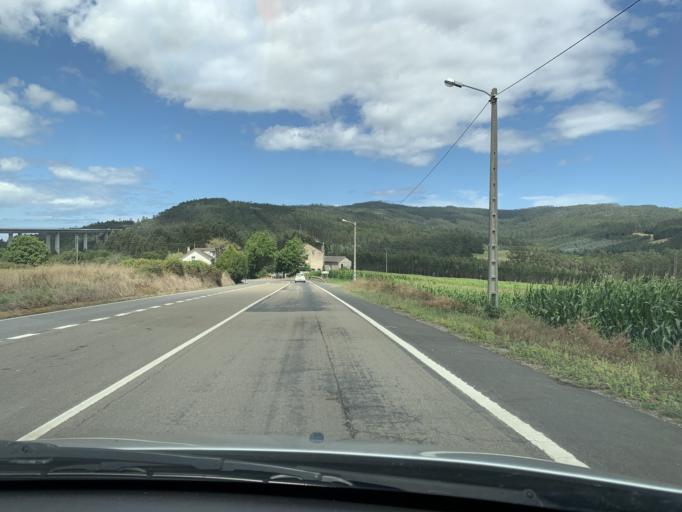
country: ES
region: Galicia
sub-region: Provincia de Lugo
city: Barreiros
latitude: 43.4991
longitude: -7.2700
